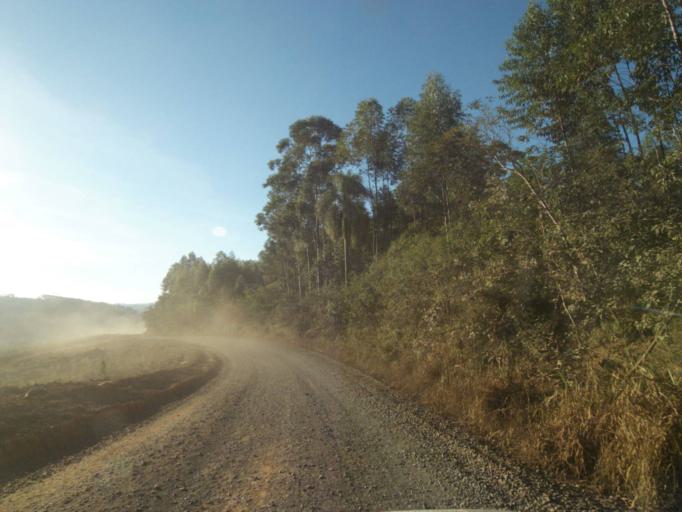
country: BR
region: Parana
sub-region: Telemaco Borba
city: Telemaco Borba
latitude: -24.4218
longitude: -50.5892
